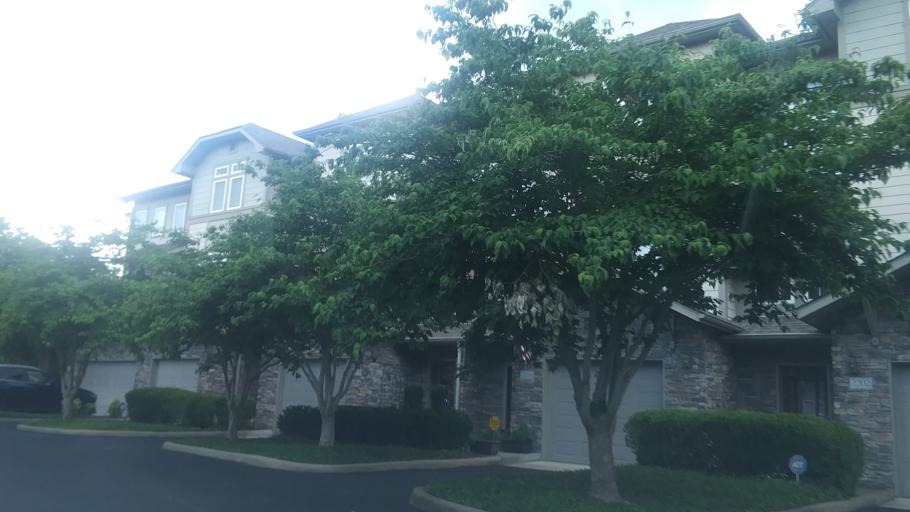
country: US
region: Tennessee
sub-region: Davidson County
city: Belle Meade
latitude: 36.0904
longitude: -86.9174
